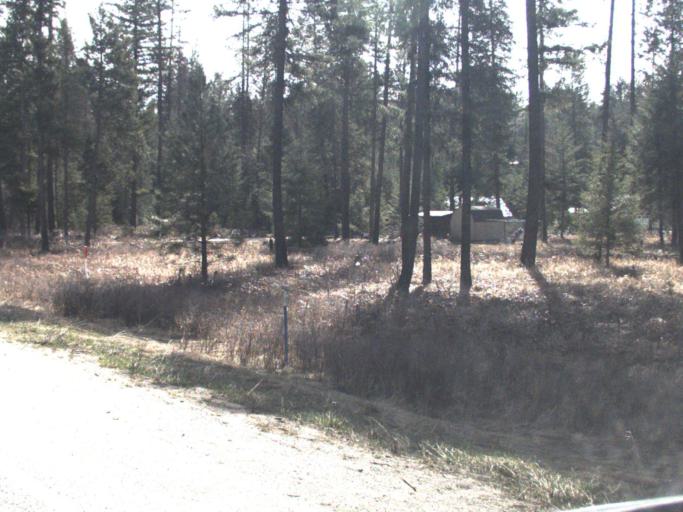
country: US
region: Washington
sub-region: Stevens County
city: Colville
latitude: 48.5403
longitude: -117.8358
